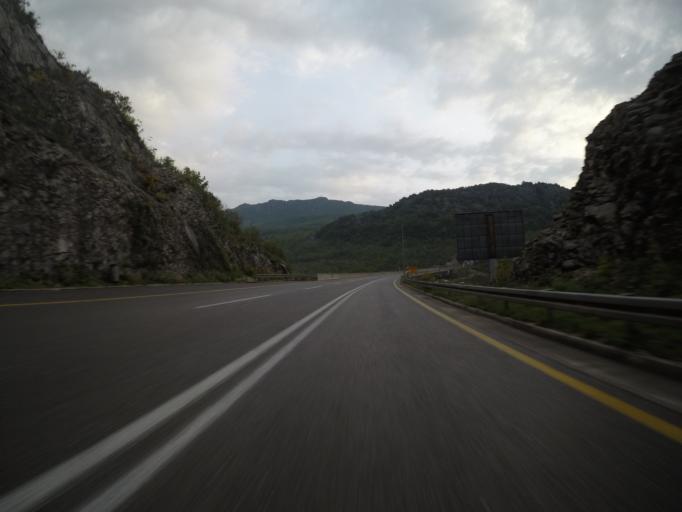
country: ME
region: Bar
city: Sutomore
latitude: 42.2242
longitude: 19.0512
